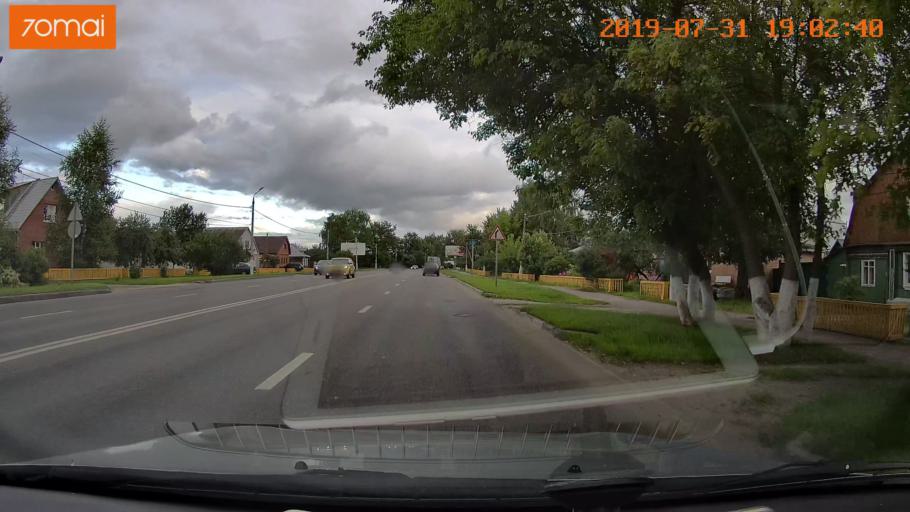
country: RU
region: Moskovskaya
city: Raduzhnyy
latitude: 55.1193
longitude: 38.7337
